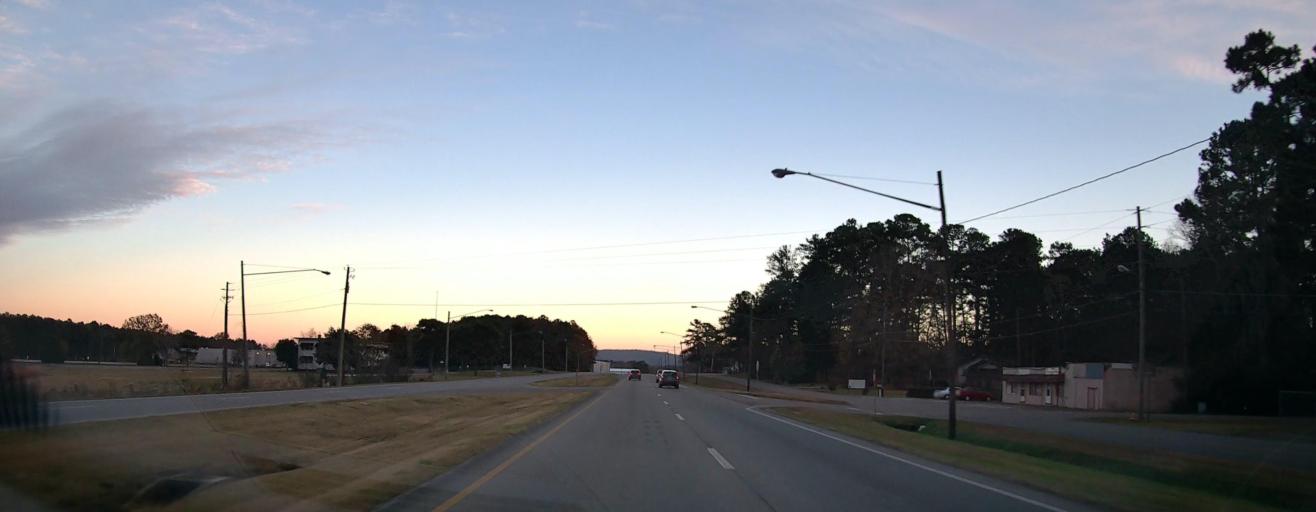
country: US
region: Alabama
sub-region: Etowah County
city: Glencoe
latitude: 33.9844
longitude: -85.9628
